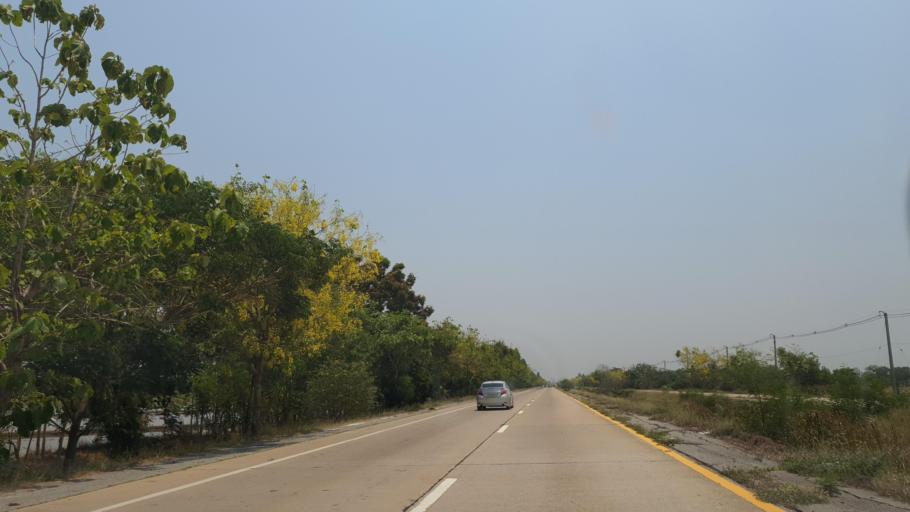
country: TH
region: Suphan Buri
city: Suphan Buri
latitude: 14.5508
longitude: 100.0859
